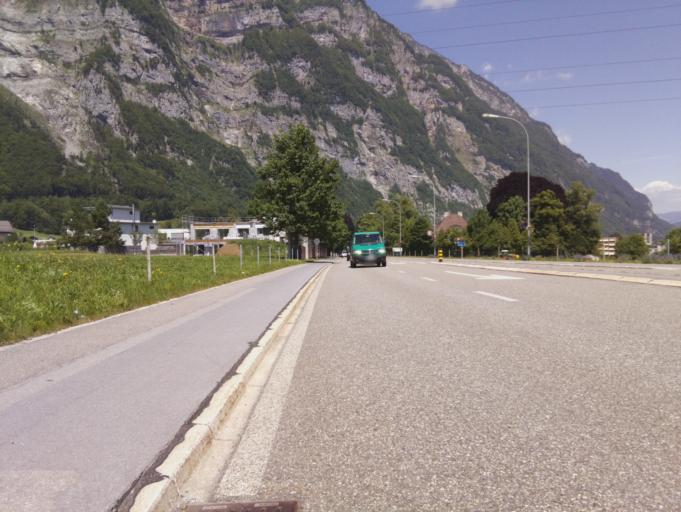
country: CH
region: Glarus
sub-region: Glarus
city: Netstal
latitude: 47.0550
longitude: 9.0552
